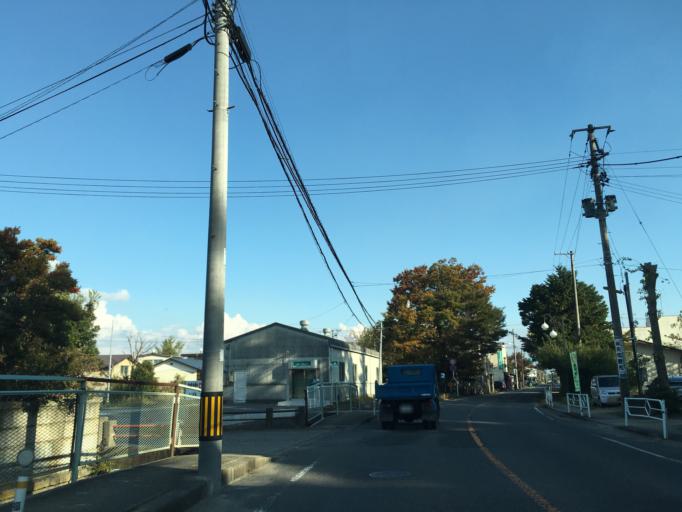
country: JP
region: Fukushima
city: Koriyama
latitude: 37.3972
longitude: 140.2712
